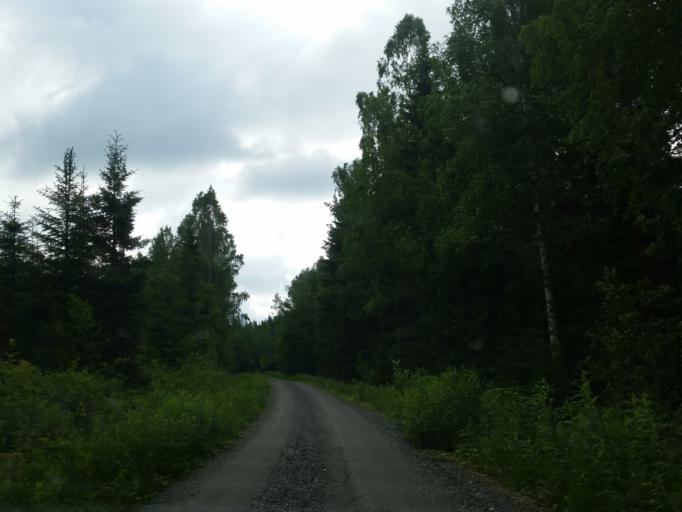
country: FI
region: Northern Savo
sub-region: Sisae-Savo
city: Tervo
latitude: 63.0561
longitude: 26.6770
